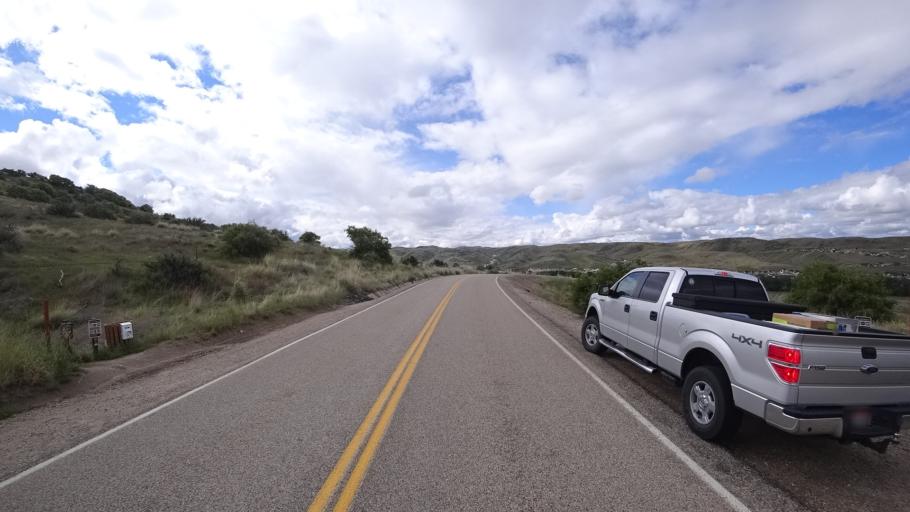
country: US
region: Idaho
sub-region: Ada County
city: Garden City
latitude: 43.7212
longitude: -116.2344
